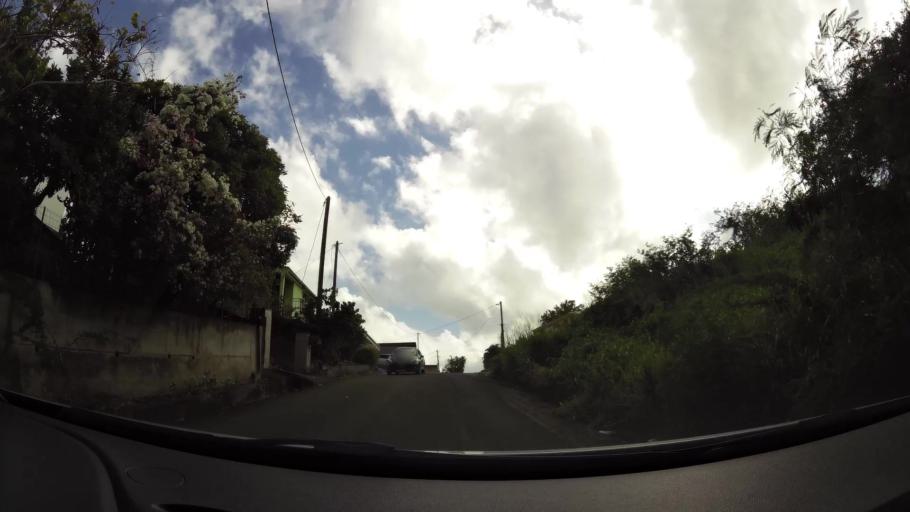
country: MQ
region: Martinique
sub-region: Martinique
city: Le Marin
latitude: 14.4630
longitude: -60.8513
